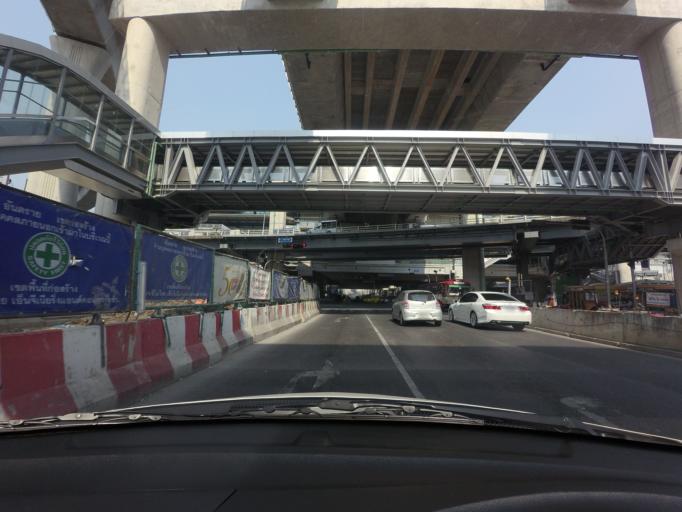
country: TH
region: Bangkok
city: Bangkok Yai
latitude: 13.7290
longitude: 100.4743
